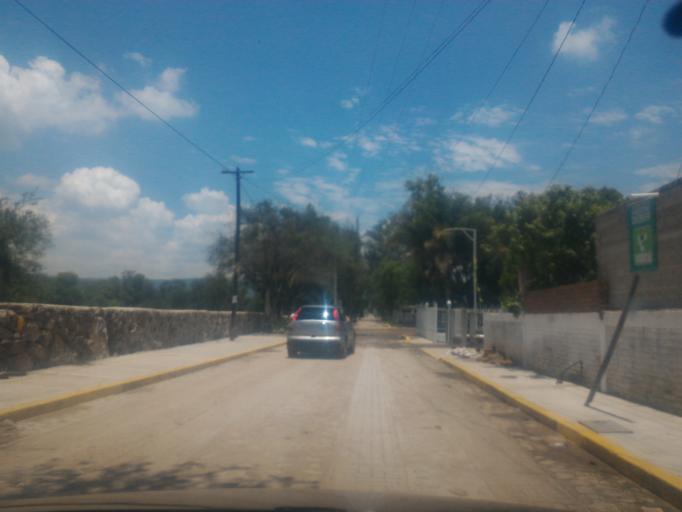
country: MX
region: Guanajuato
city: Ciudad Manuel Doblado
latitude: 20.7962
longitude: -101.9963
